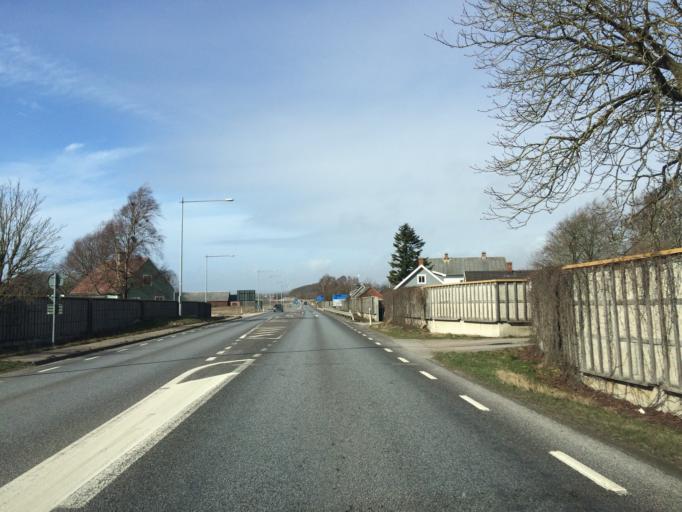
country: SE
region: Halland
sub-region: Halmstads Kommun
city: Paarp
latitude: 56.5947
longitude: 12.9770
